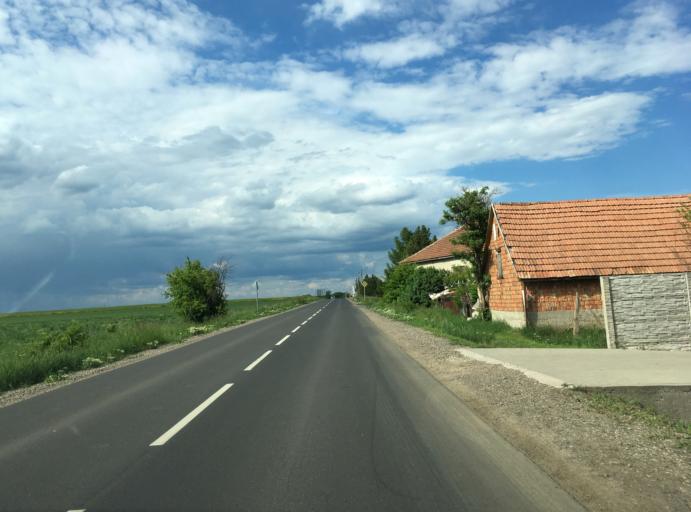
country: HU
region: Heves
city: Hered
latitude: 47.6586
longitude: 19.6189
